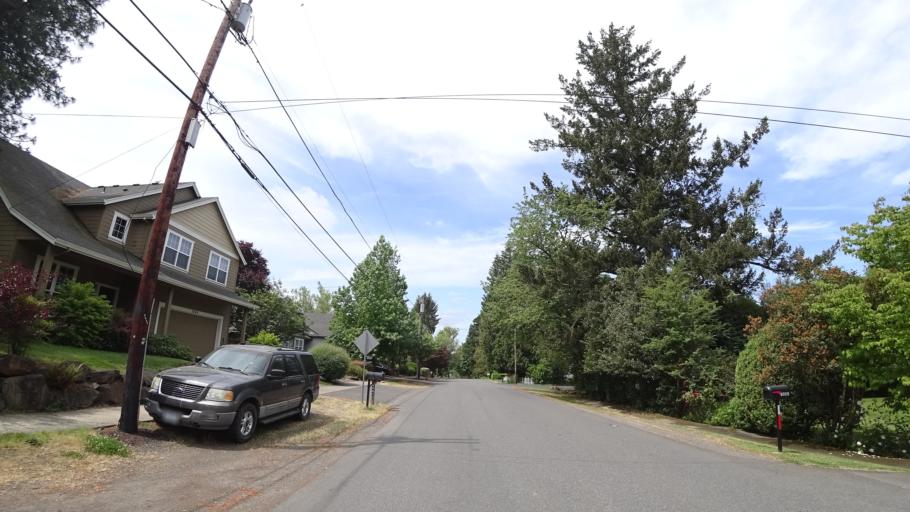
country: US
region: Oregon
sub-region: Washington County
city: Metzger
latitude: 45.4466
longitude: -122.7554
